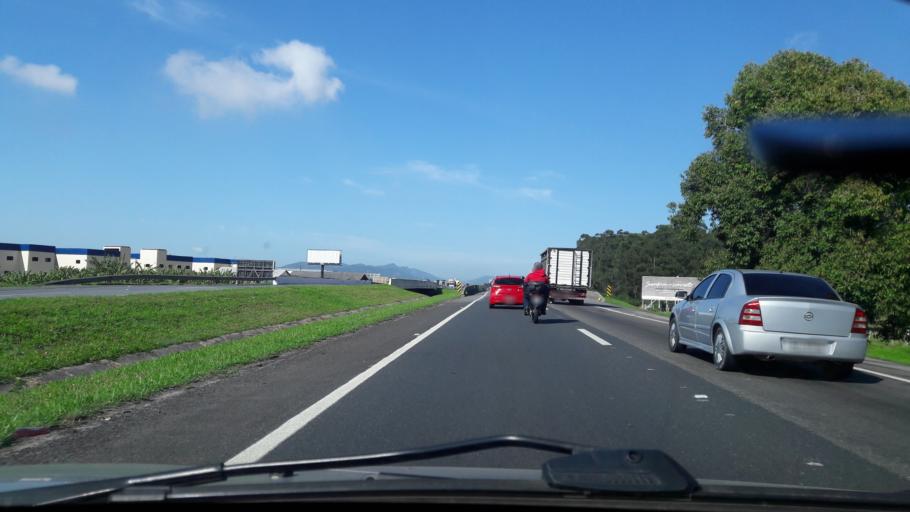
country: BR
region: Santa Catarina
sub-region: Tijucas
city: Tijucas
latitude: -27.2104
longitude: -48.6209
